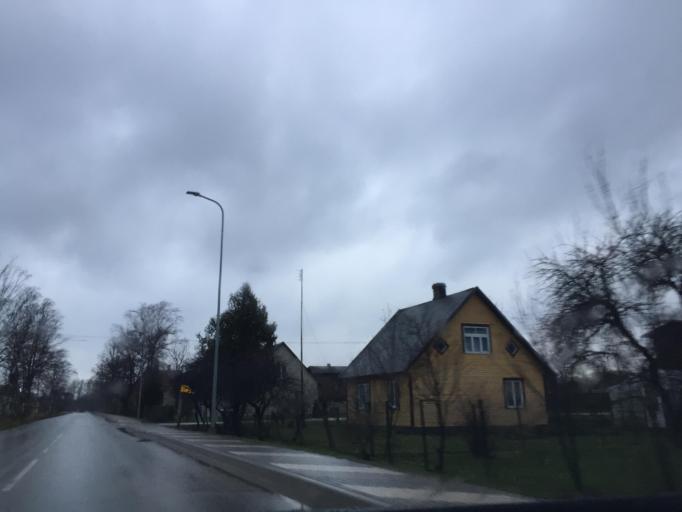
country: LV
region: Salacgrivas
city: Salacgriva
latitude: 57.7491
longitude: 24.3650
